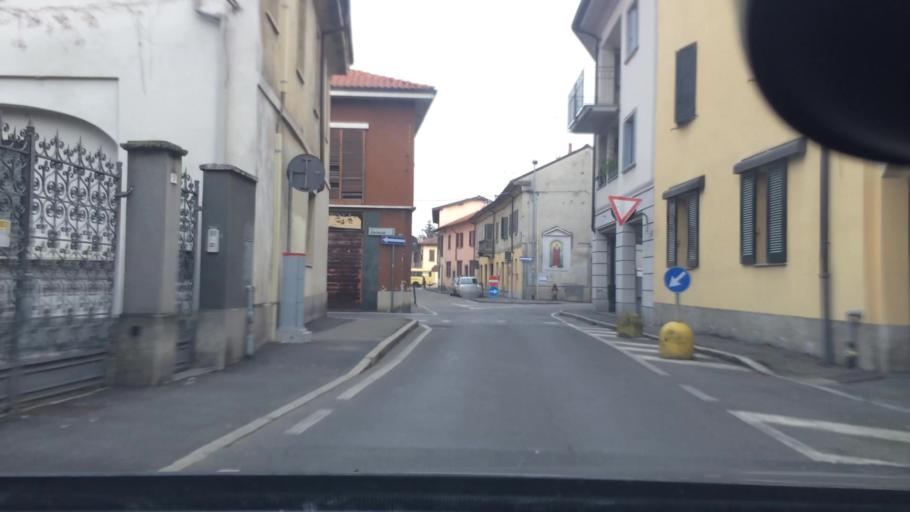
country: IT
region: Lombardy
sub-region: Provincia di Como
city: Rovellasca
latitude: 45.6663
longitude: 9.0531
